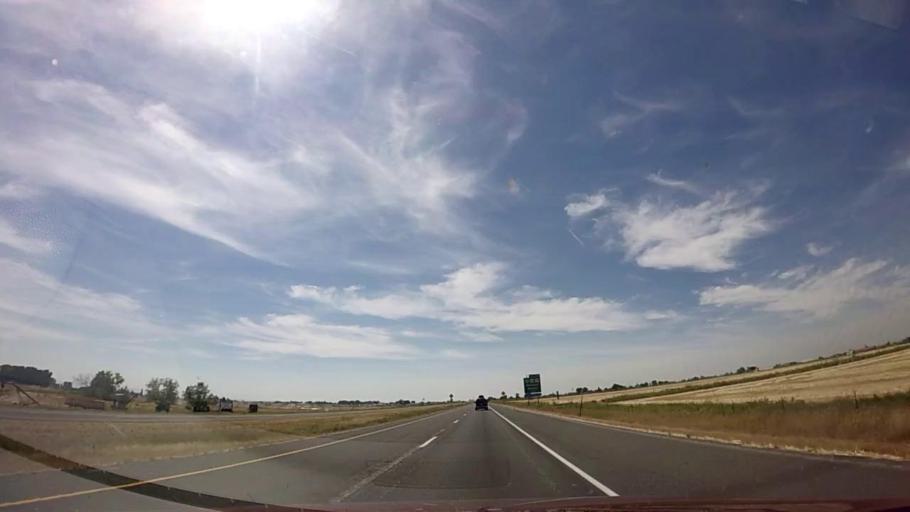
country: US
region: Idaho
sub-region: Minidoka County
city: Heyburn
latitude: 42.5691
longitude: -113.7094
